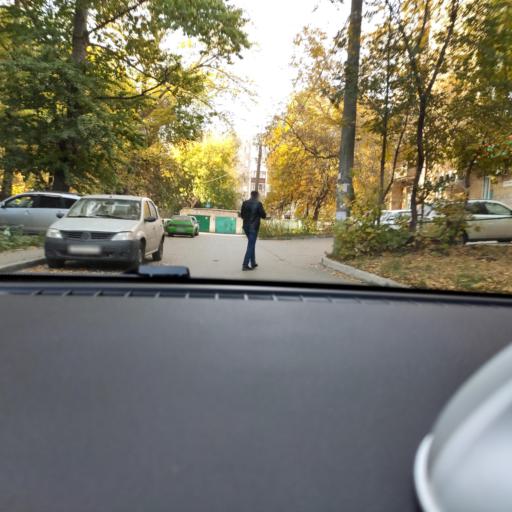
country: RU
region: Samara
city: Samara
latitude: 53.2389
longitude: 50.2372
